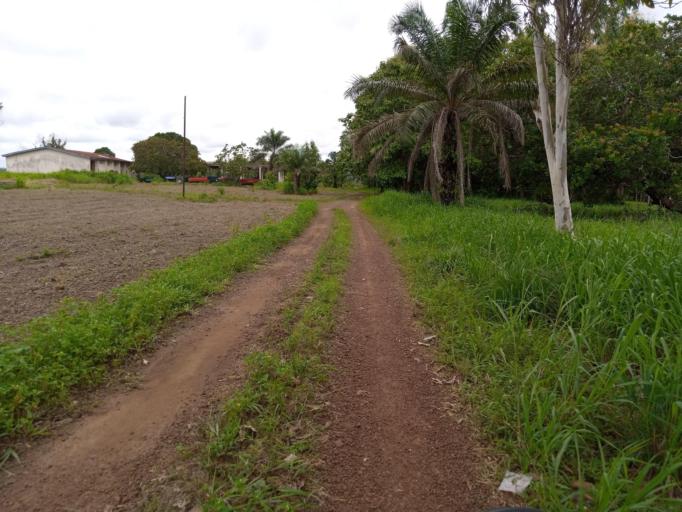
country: SL
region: Southern Province
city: Moyamba
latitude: 8.1705
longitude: -12.4197
